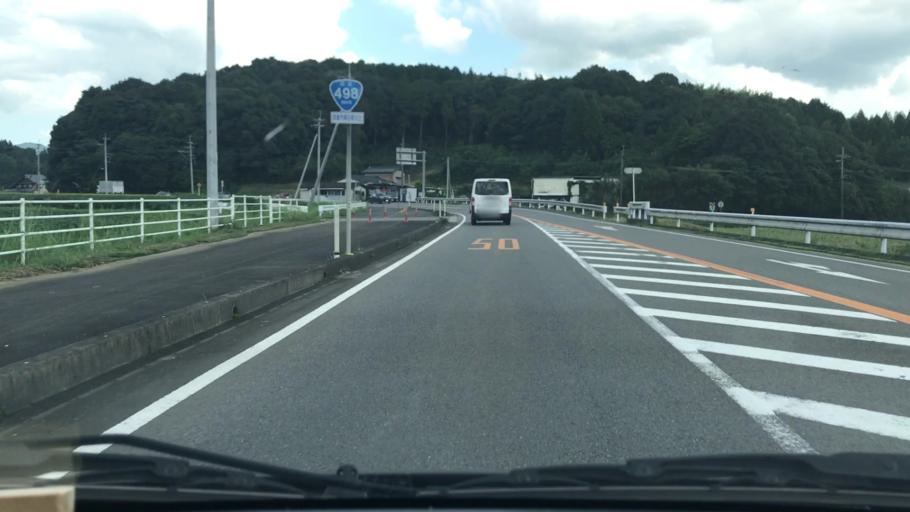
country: JP
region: Saga Prefecture
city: Takeocho-takeo
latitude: 33.2261
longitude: 130.0256
